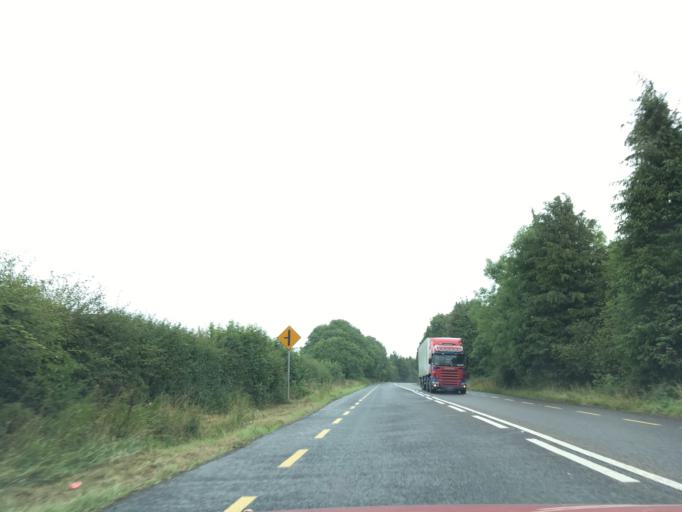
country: IE
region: Munster
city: Carrick-on-Suir
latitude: 52.3644
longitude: -7.5104
